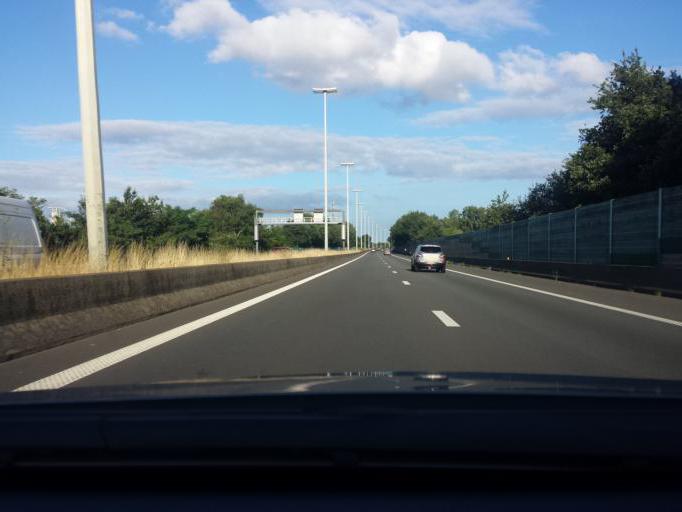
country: BE
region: Flanders
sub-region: Provincie Antwerpen
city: Olen
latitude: 51.1436
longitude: 4.8955
